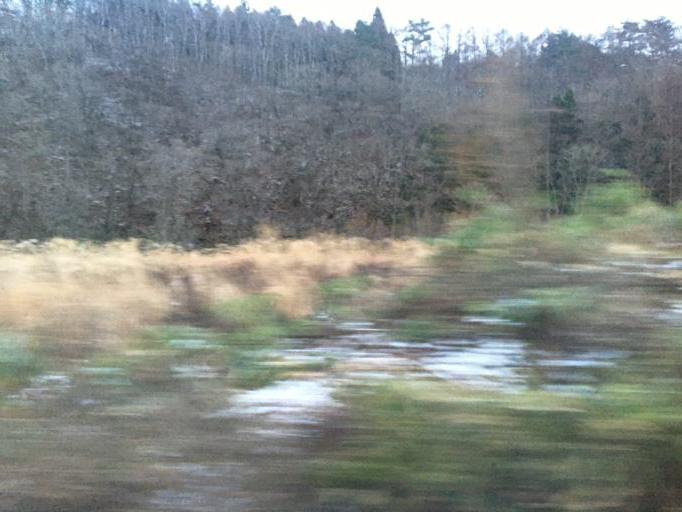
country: JP
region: Aomori
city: Aomori Shi
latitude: 40.8138
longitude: 140.6466
